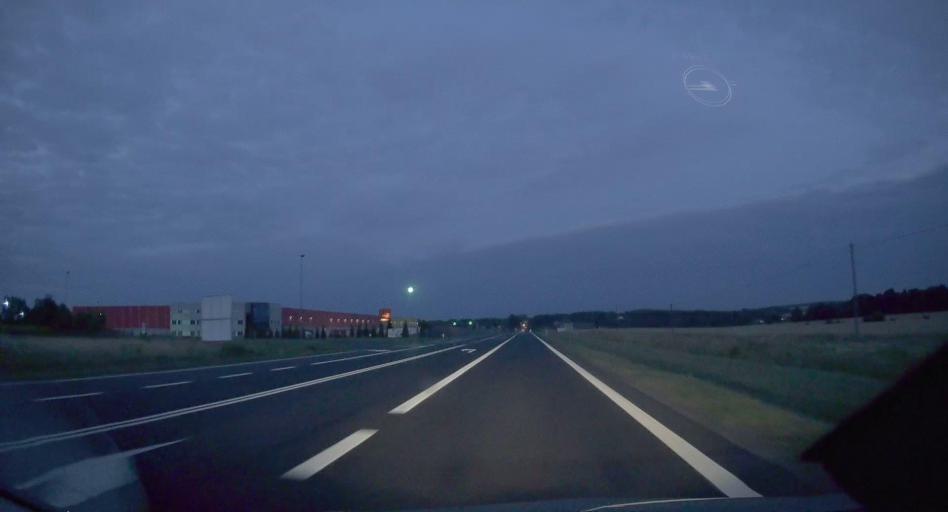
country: PL
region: Silesian Voivodeship
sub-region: Powiat klobucki
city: Klobuck
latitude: 50.8873
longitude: 18.9756
